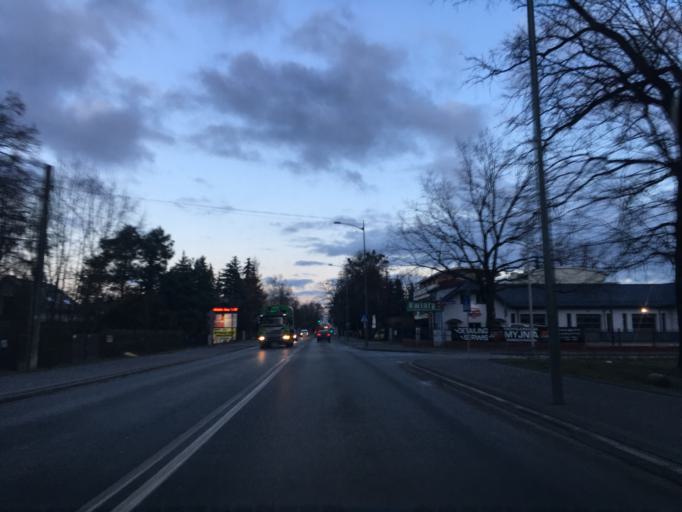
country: PL
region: Masovian Voivodeship
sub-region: Powiat grodziski
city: Grodzisk Mazowiecki
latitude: 52.1078
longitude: 20.6323
